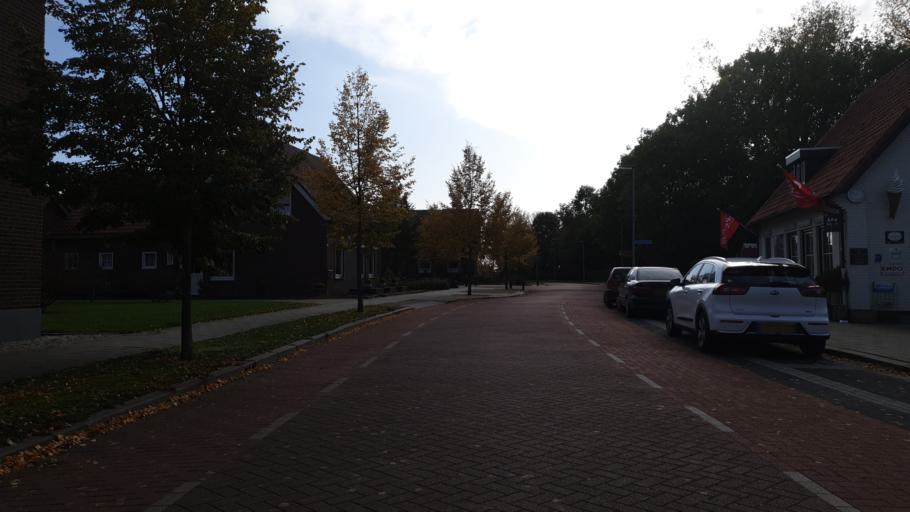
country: NL
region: Limburg
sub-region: Gemeente Gennep
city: Gennep
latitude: 51.6732
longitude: 5.9776
